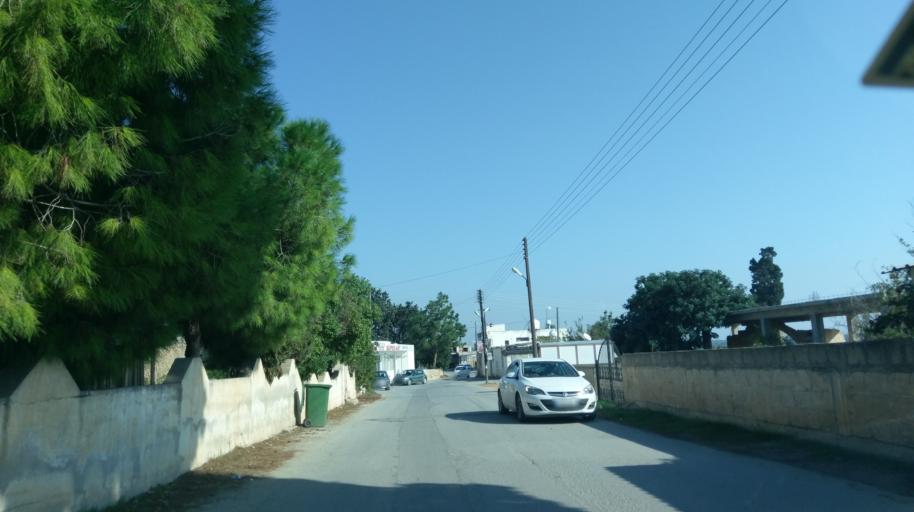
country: CY
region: Ammochostos
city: Leonarisso
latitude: 35.4724
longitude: 34.1502
